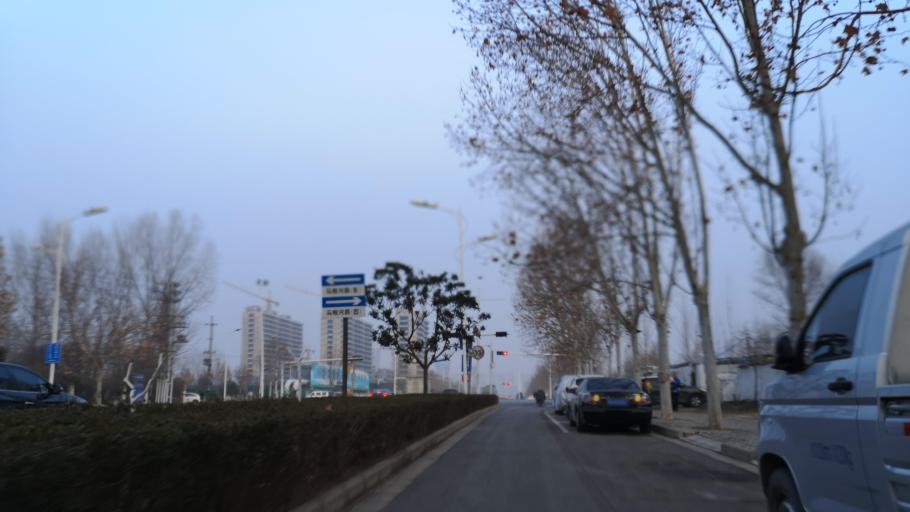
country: CN
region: Henan Sheng
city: Puyang
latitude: 35.7485
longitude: 115.0389
